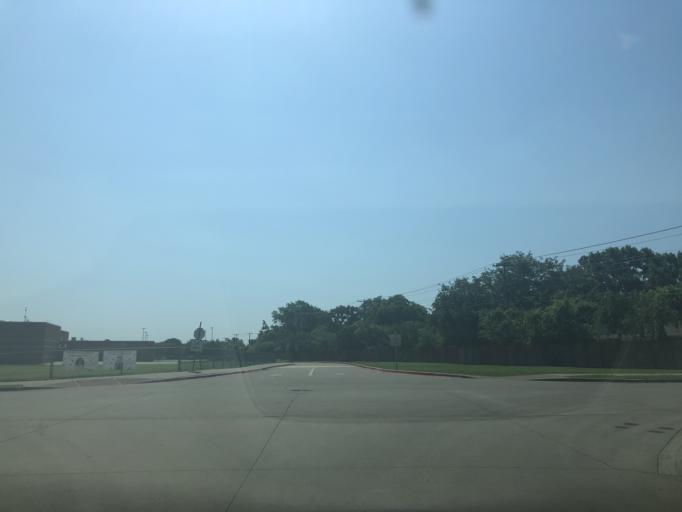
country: US
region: Texas
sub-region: Dallas County
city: Grand Prairie
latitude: 32.7250
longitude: -97.0016
